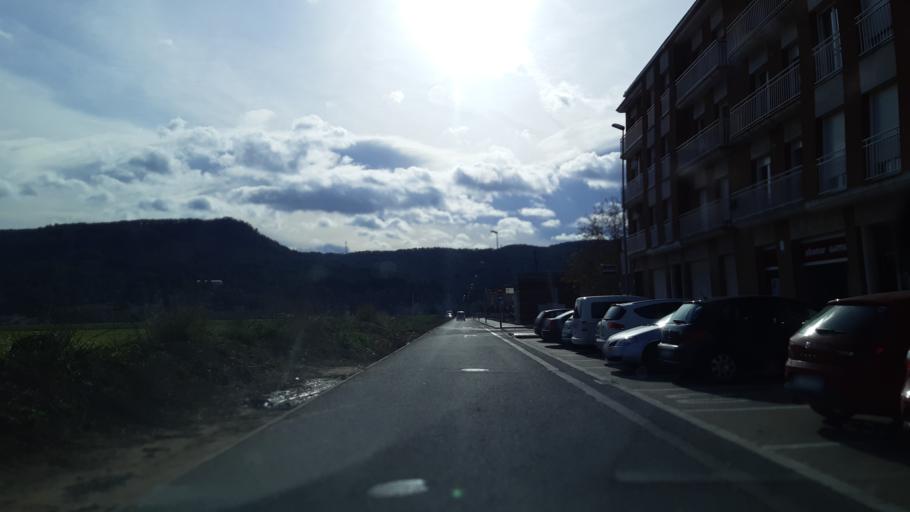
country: ES
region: Catalonia
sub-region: Provincia de Barcelona
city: Vilanova del Cami
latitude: 41.5690
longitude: 1.6438
